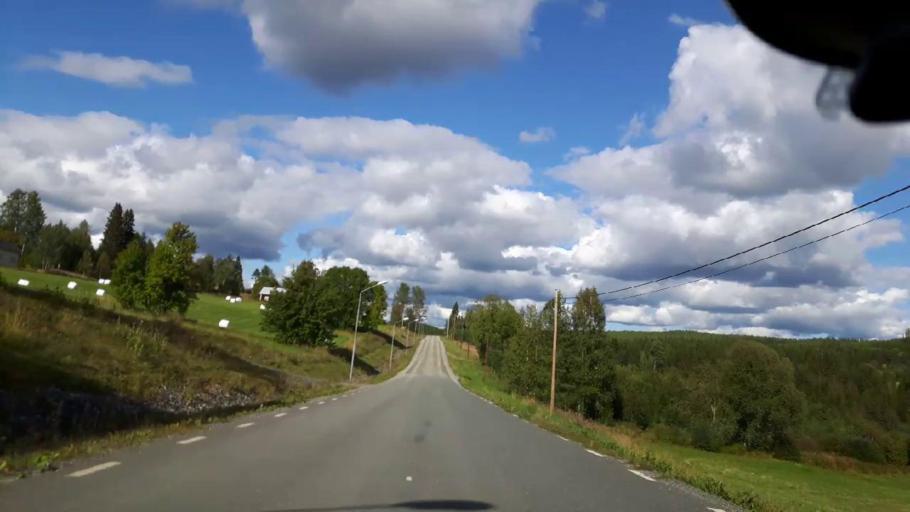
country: SE
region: Jaemtland
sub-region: Stroemsunds Kommun
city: Stroemsund
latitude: 63.3010
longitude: 15.6021
